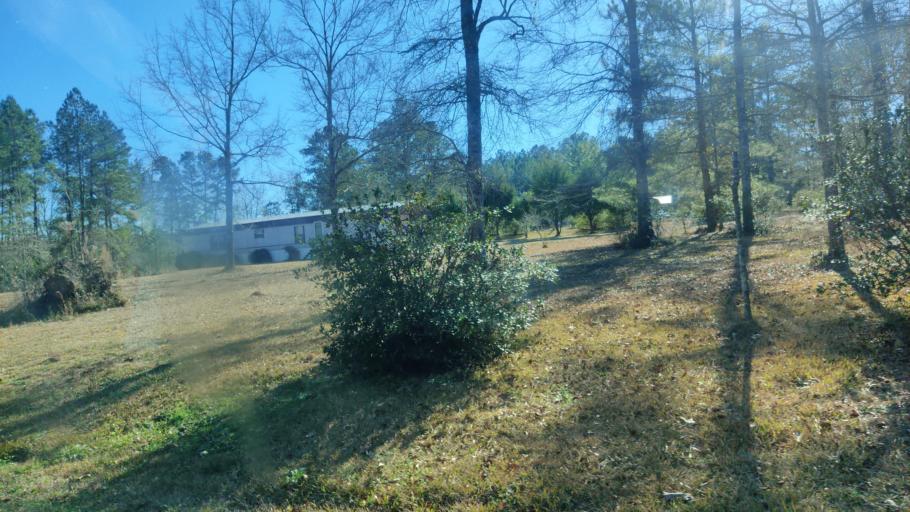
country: US
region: Mississippi
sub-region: Jones County
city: Ellisville
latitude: 31.5471
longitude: -89.3314
